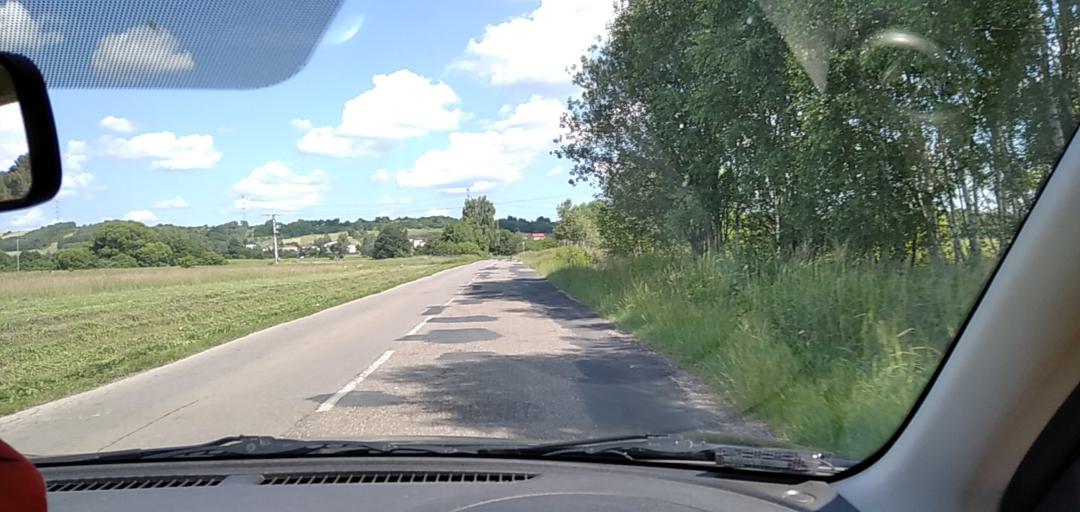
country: PL
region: Silesian Voivodeship
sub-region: Powiat bedzinski
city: Sarnow
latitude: 50.3970
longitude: 19.1384
